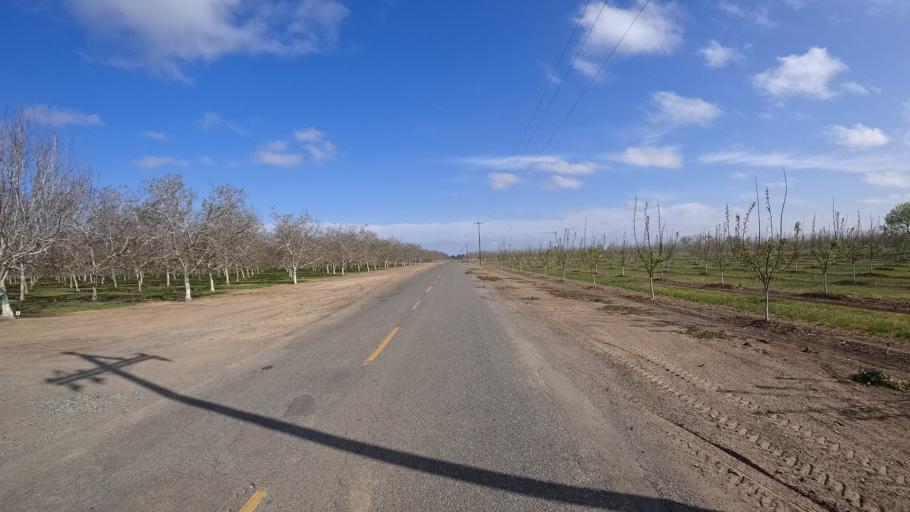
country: US
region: California
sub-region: Glenn County
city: Willows
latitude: 39.4788
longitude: -121.9677
